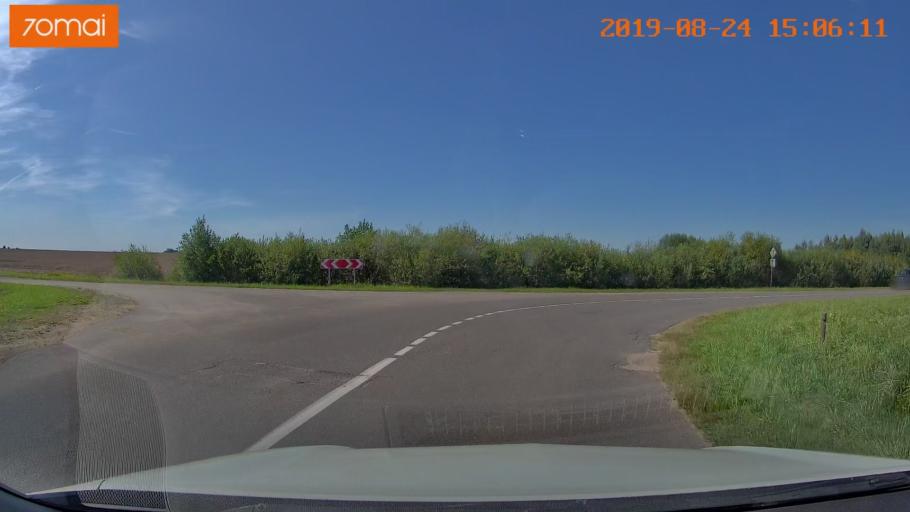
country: BY
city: Michanovichi
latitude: 53.5992
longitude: 27.6772
